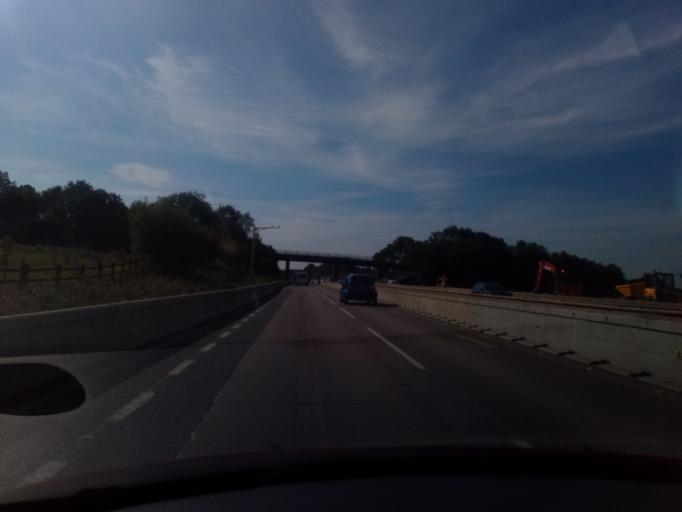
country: GB
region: England
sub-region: Stockton-on-Tees
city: Billingham
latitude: 54.6225
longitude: -1.3142
